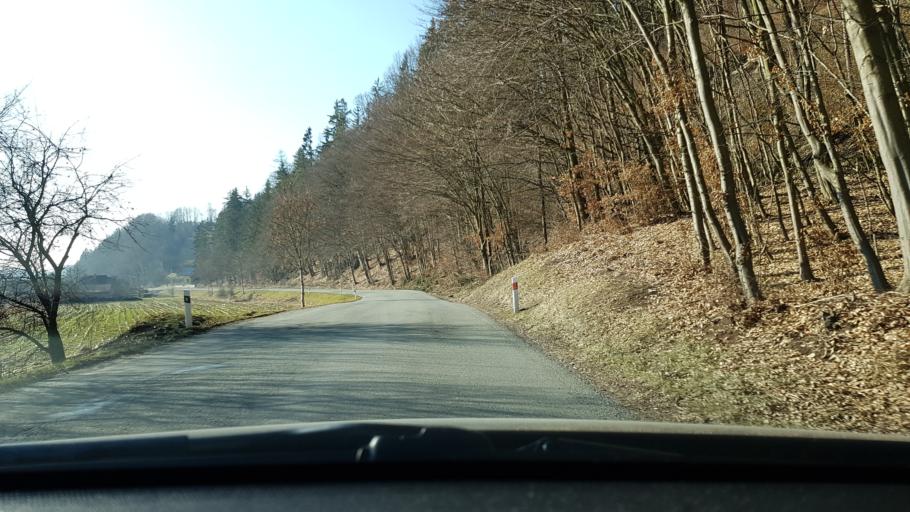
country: CZ
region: Olomoucky
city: Dolni Bohdikov
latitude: 50.0126
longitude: 16.8956
